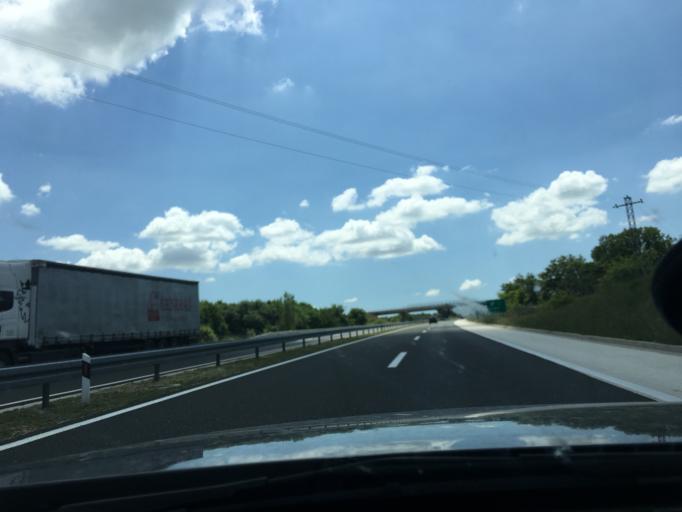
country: HR
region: Zadarska
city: Posedarje
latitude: 44.2043
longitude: 15.4442
